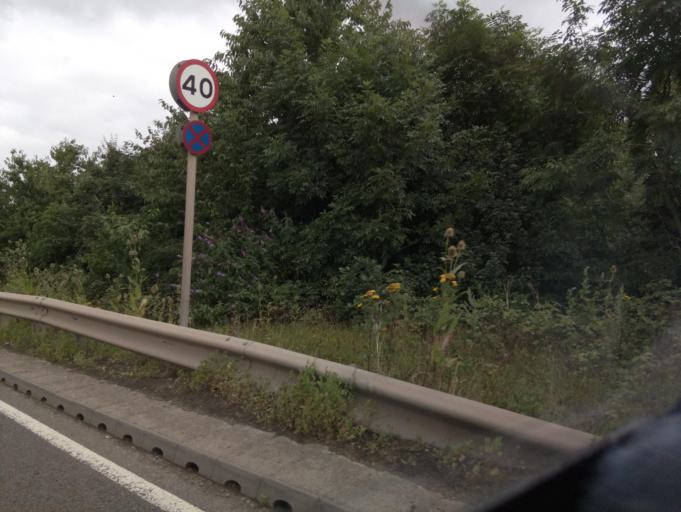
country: GB
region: England
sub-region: Nottinghamshire
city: Burton Joyce
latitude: 52.9714
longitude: -1.0607
